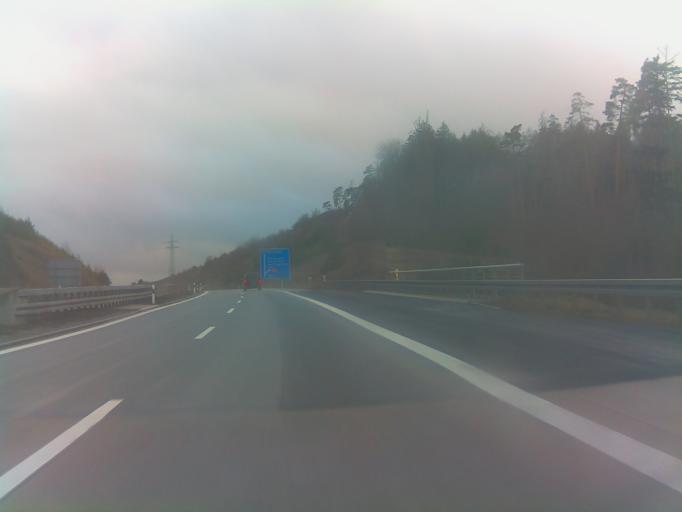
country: DE
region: Bavaria
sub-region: Regierungsbezirk Unterfranken
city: Hollstadt
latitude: 50.3361
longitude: 10.2993
